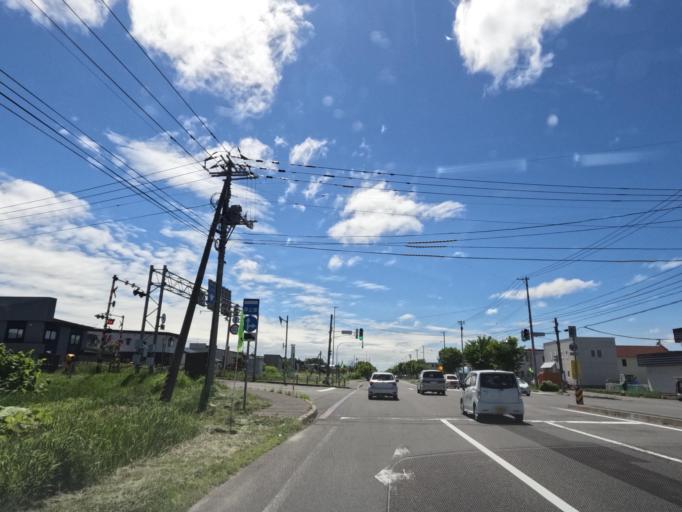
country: JP
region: Hokkaido
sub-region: Asahikawa-shi
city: Asahikawa
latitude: 43.7401
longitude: 142.3603
